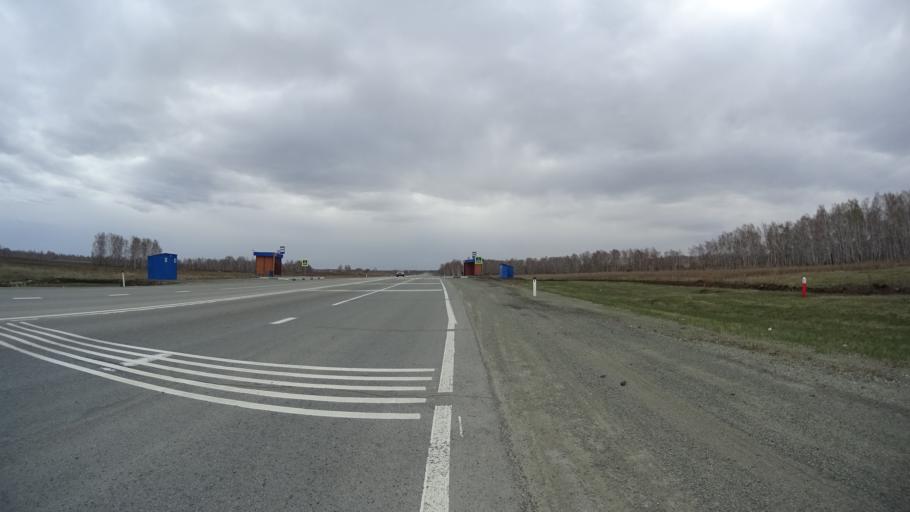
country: RU
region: Chelyabinsk
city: Yemanzhelinsk
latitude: 54.6969
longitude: 61.2500
